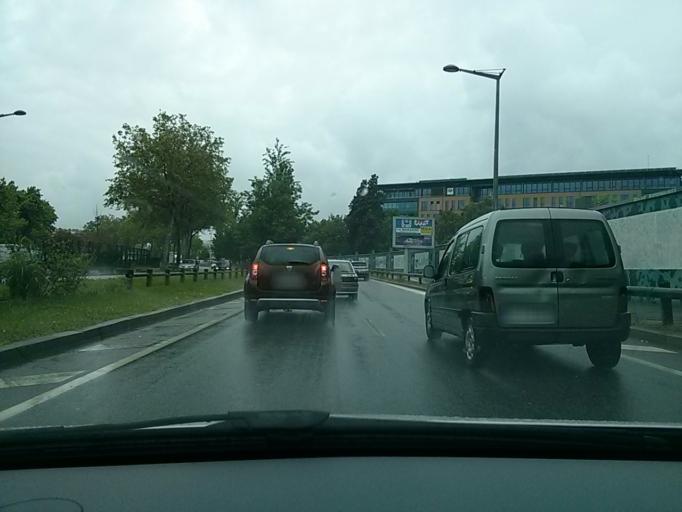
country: FR
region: Rhone-Alpes
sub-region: Departement du Rhone
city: Saint-Fons
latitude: 45.7245
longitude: 4.8420
